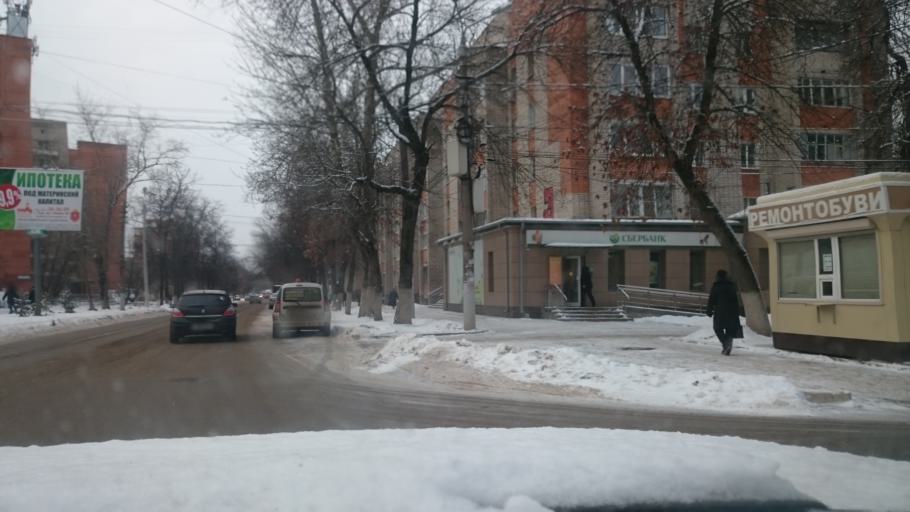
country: RU
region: Tula
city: Mendeleyevskiy
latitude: 54.1692
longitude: 37.5827
